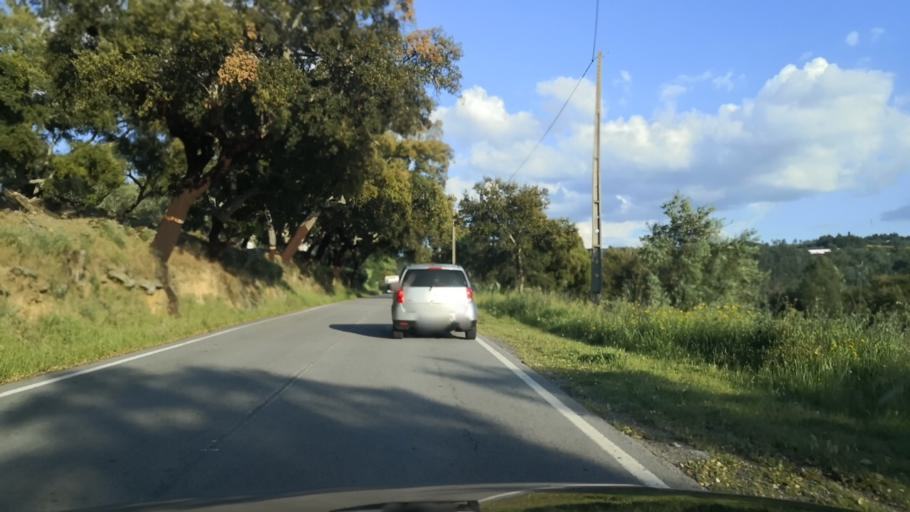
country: PT
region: Portalegre
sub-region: Portalegre
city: Portalegre
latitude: 39.3267
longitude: -7.4240
